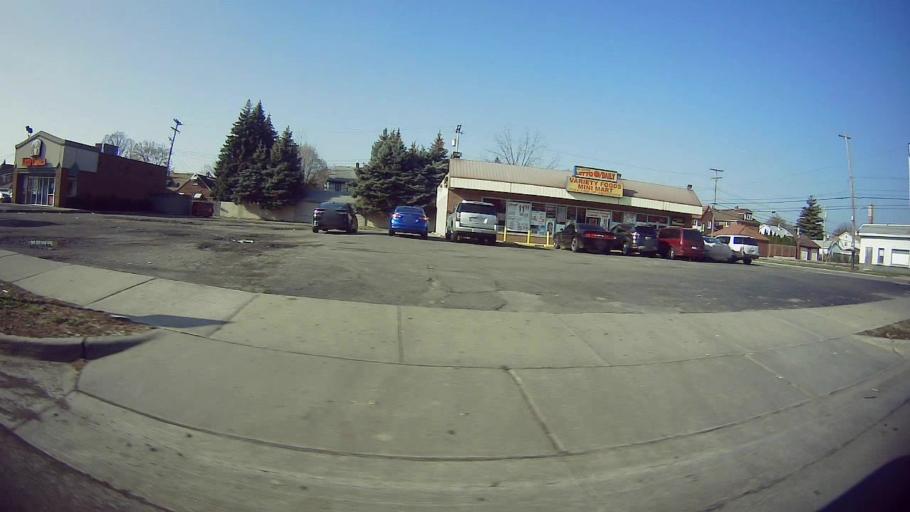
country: US
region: Michigan
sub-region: Wayne County
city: Dearborn
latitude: 42.3450
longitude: -83.1770
